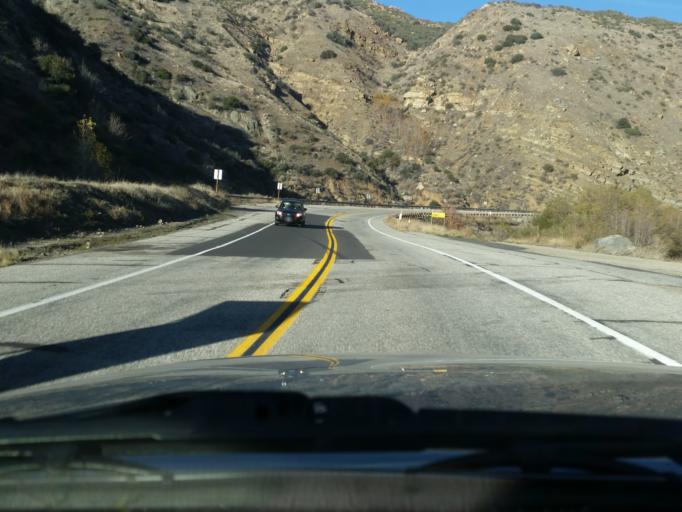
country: US
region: California
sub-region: San Bernardino County
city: Yucaipa
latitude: 34.0942
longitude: -117.0337
